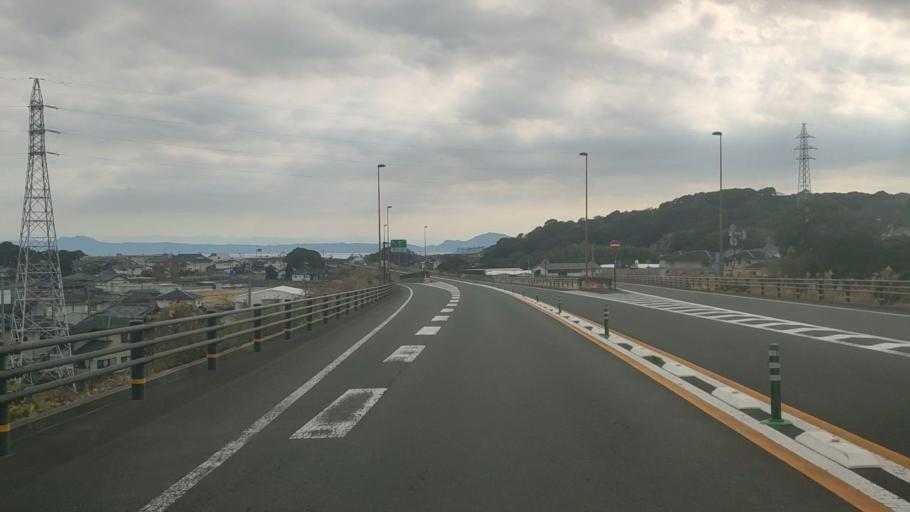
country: JP
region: Nagasaki
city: Shimabara
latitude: 32.7639
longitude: 130.3615
